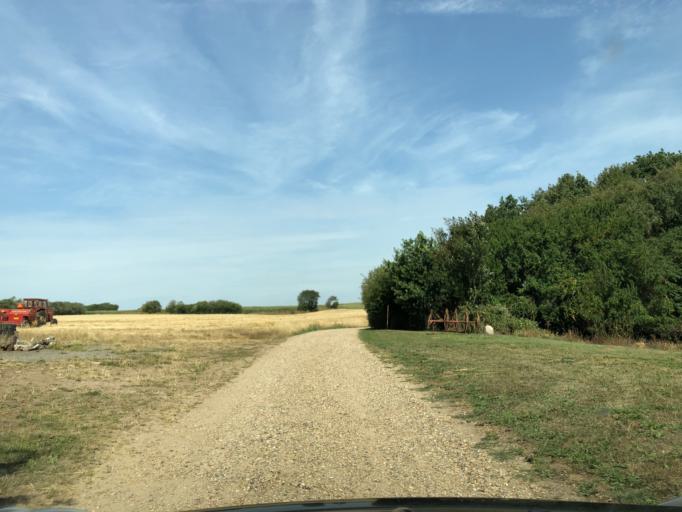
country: DK
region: Central Jutland
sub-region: Ringkobing-Skjern Kommune
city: Skjern
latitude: 55.9962
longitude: 8.4969
